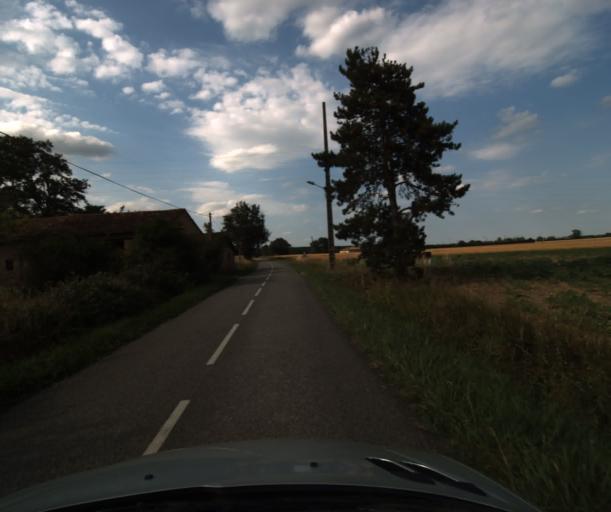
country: FR
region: Midi-Pyrenees
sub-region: Departement de la Haute-Garonne
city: Fonsorbes
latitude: 43.5248
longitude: 1.2321
